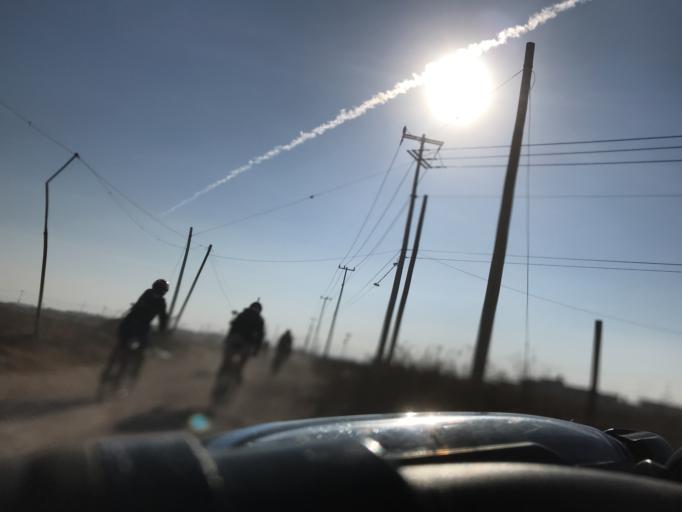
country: MX
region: Mexico
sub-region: Nextlalpan
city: Ex-Hacienda Santa Ines
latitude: 19.6966
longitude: -99.0730
